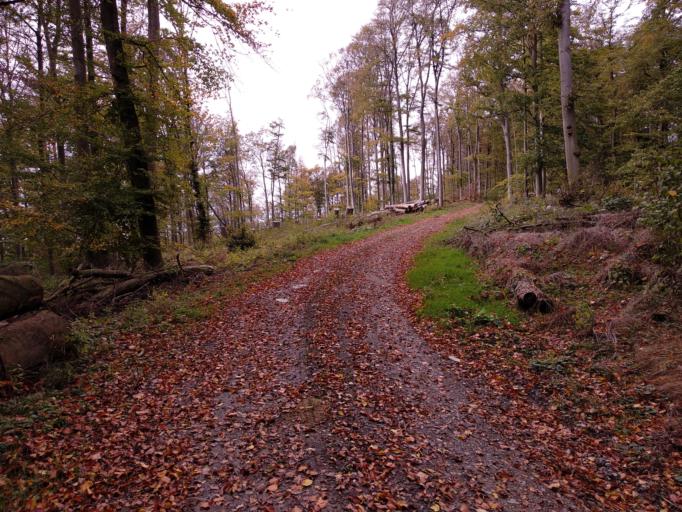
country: DE
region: North Rhine-Westphalia
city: Beverungen
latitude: 51.6681
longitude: 9.3622
